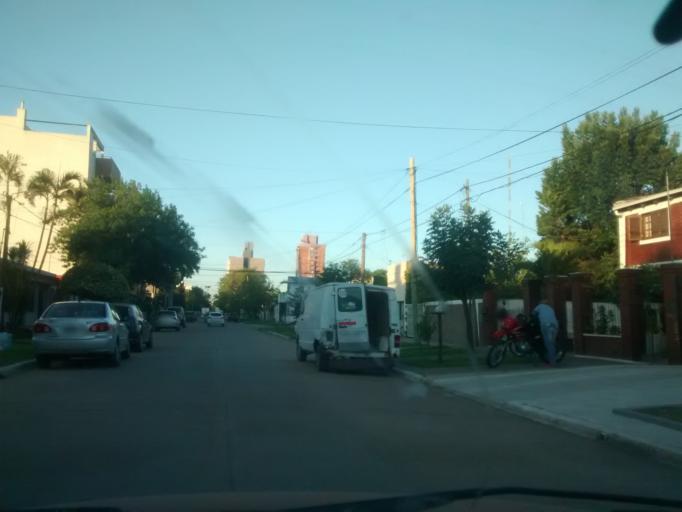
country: AR
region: Chaco
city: Resistencia
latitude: -27.4579
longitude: -58.9974
